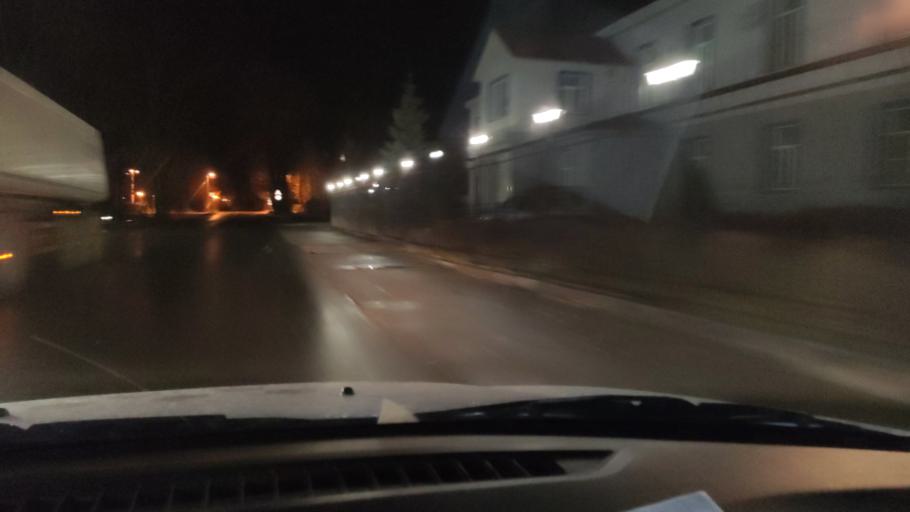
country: RU
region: Perm
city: Overyata
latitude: 58.0176
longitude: 55.9106
